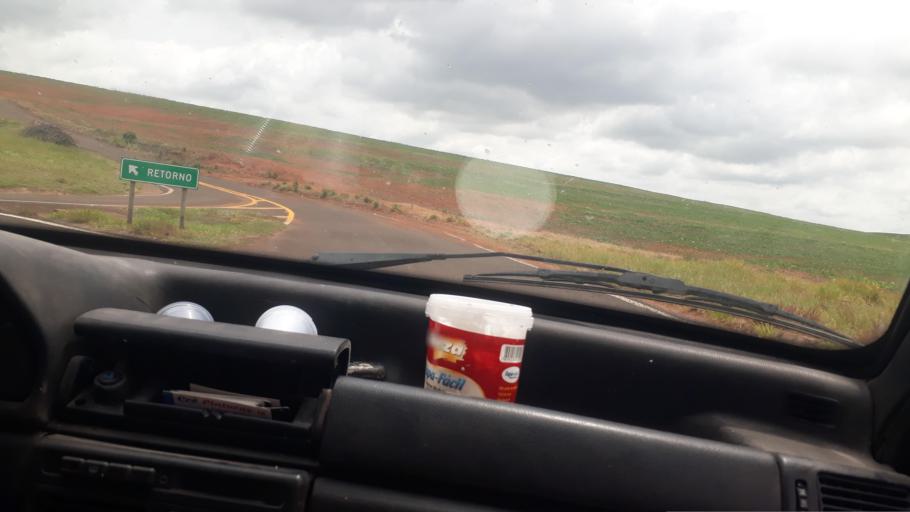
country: BR
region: Sao Paulo
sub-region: Regente Feijo
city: Regente Feijo
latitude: -22.2646
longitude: -51.3034
